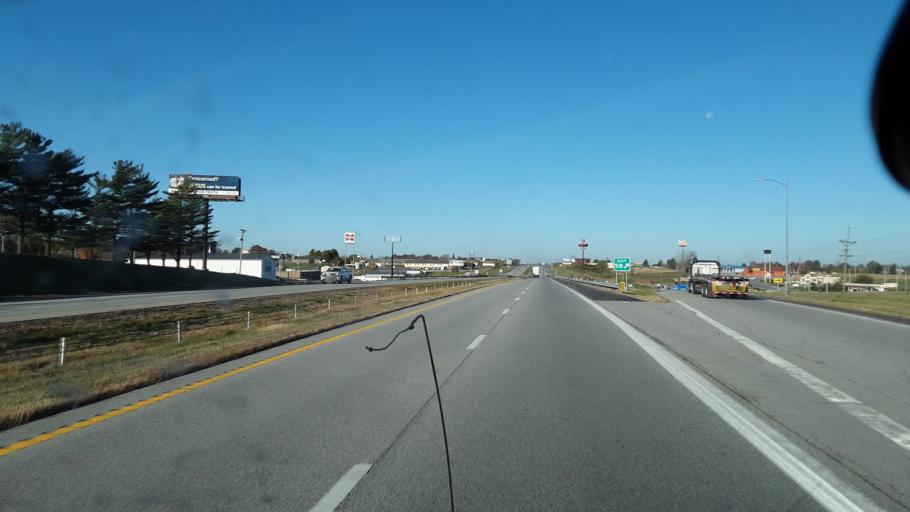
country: US
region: Missouri
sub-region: Lafayette County
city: Concordia
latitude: 38.9917
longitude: -93.5637
